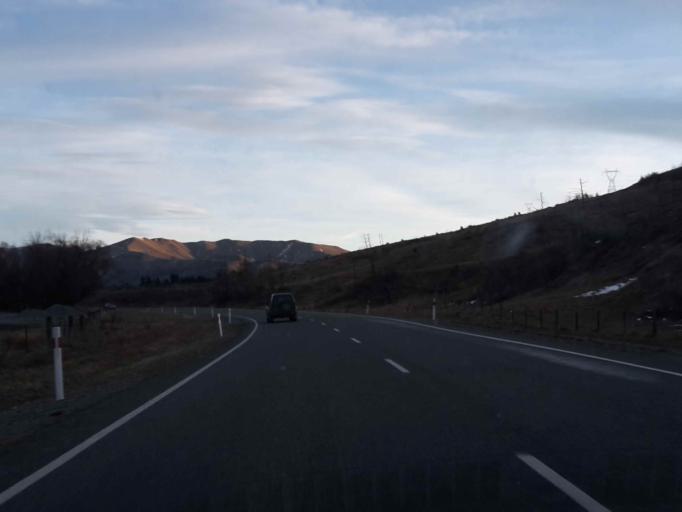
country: NZ
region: Canterbury
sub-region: Timaru District
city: Pleasant Point
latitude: -44.0698
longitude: 170.6686
